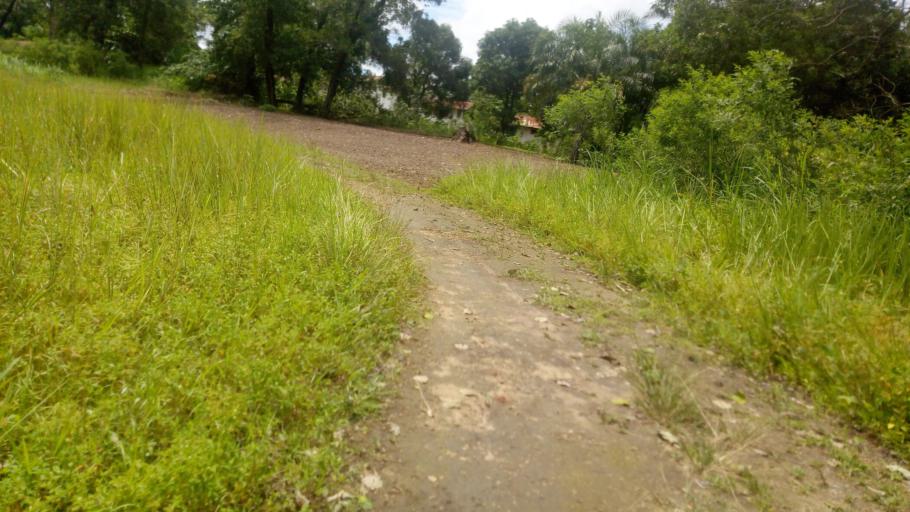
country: SL
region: Northern Province
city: Magburaka
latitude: 8.7188
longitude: -11.9464
